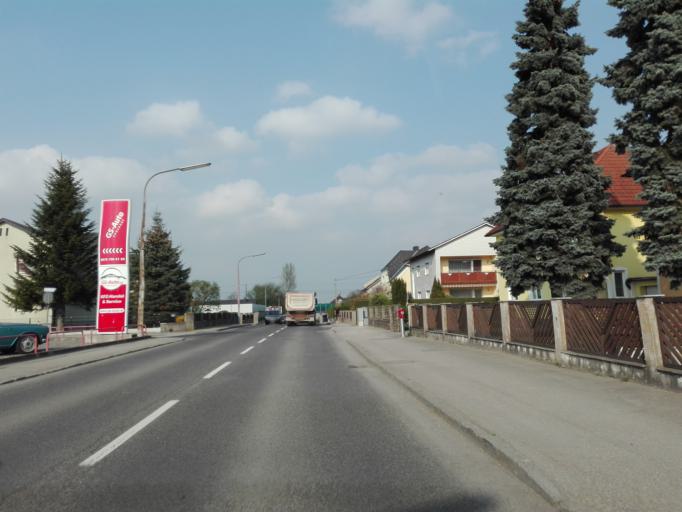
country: AT
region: Lower Austria
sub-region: Politischer Bezirk Amstetten
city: Ennsdorf
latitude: 48.2155
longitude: 14.4933
